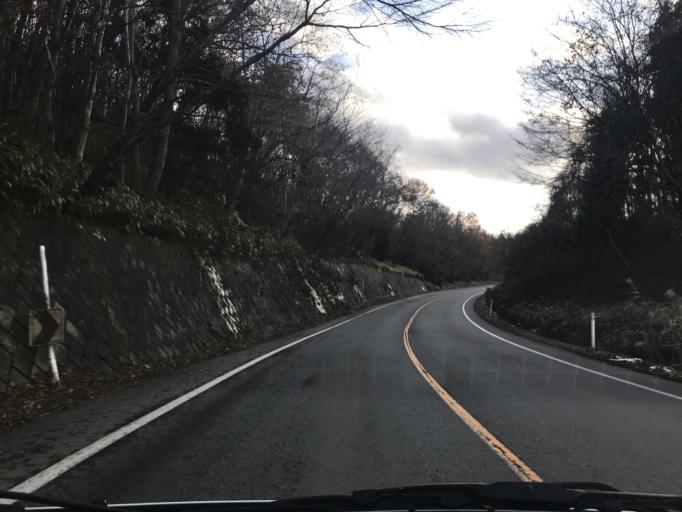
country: JP
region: Iwate
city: Mizusawa
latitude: 39.1860
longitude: 141.0538
